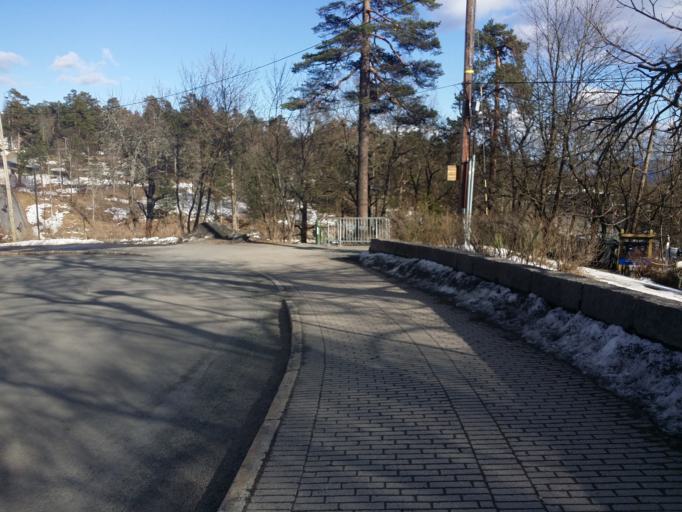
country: NO
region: Oslo
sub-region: Oslo
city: Sjolyststranda
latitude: 59.9620
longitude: 10.6653
